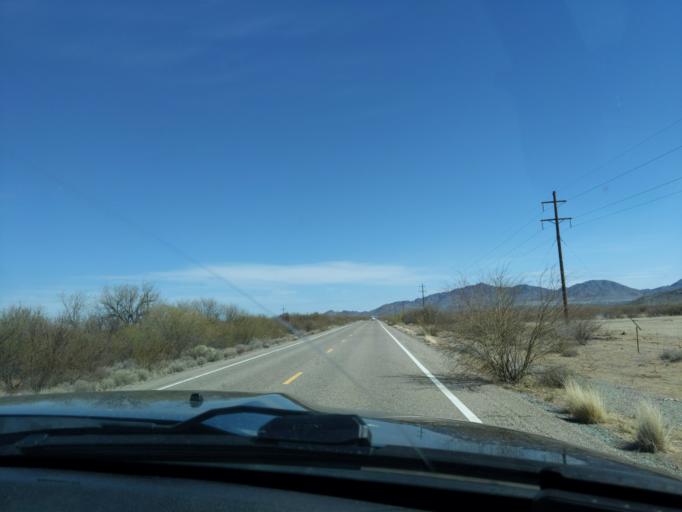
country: US
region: Arizona
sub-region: Pinal County
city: Arizona City
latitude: 32.4903
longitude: -111.9725
